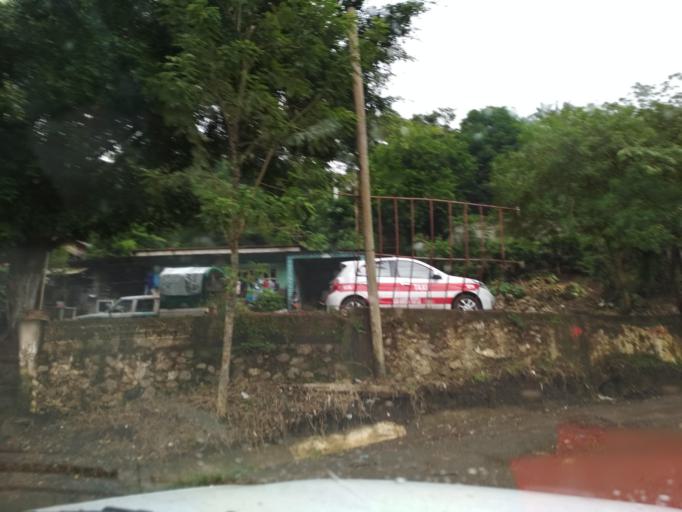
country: MX
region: Veracruz
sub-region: San Andres Tuxtla
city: San Isidro Xoteapan (San Isidro Texcaltitan)
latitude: 18.4672
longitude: -95.2382
